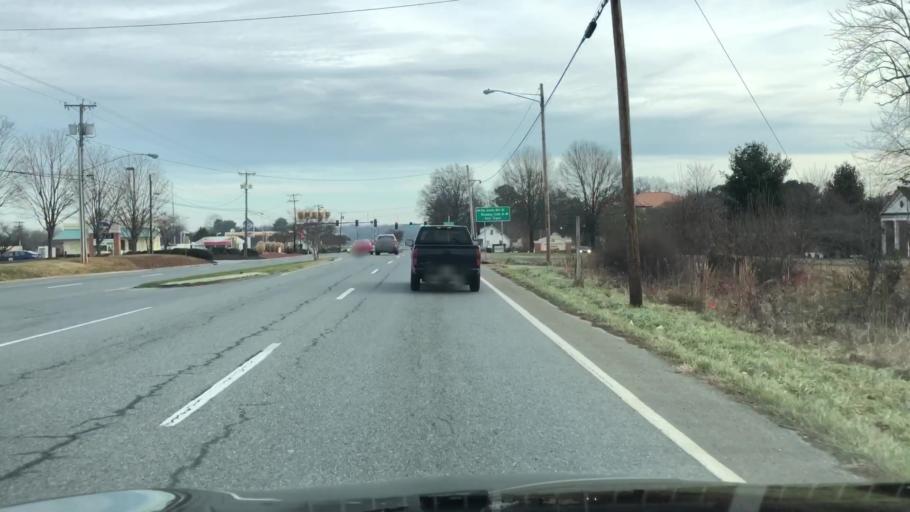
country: US
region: Virginia
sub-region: Campbell County
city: Timberlake
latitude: 37.3521
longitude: -79.2268
